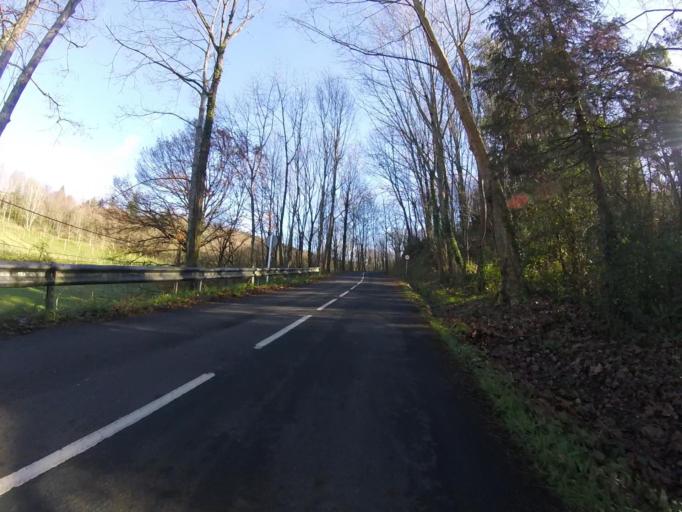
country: ES
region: Basque Country
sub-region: Provincia de Guipuzcoa
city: Irun
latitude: 43.3230
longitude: -1.7732
